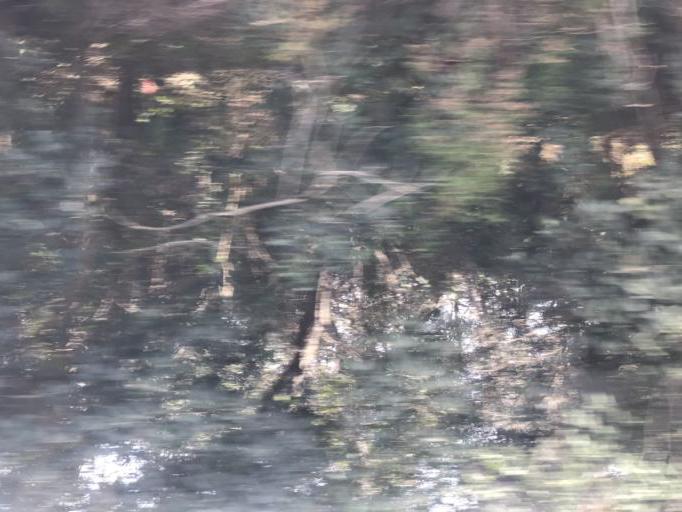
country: AR
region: Cordoba
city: Laguna Larga
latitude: -31.7871
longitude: -63.7943
